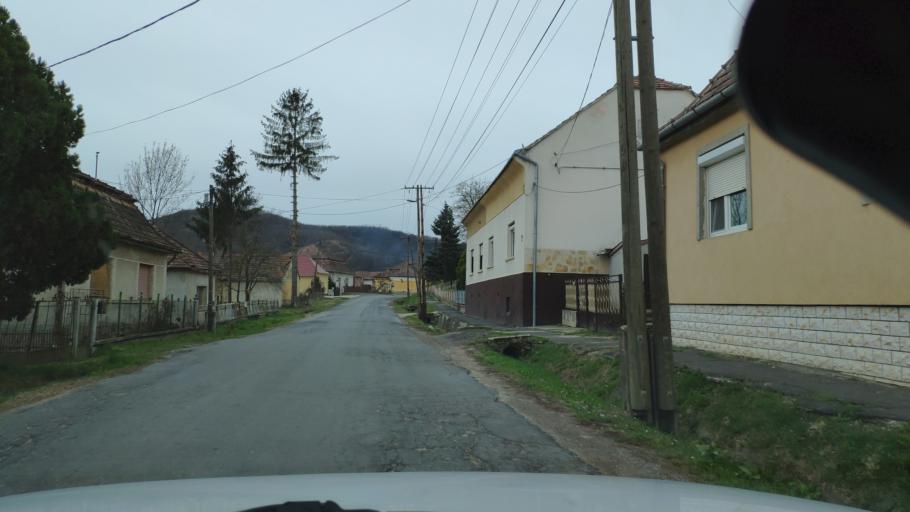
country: HU
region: Zala
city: Pacsa
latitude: 46.6739
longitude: 17.0793
